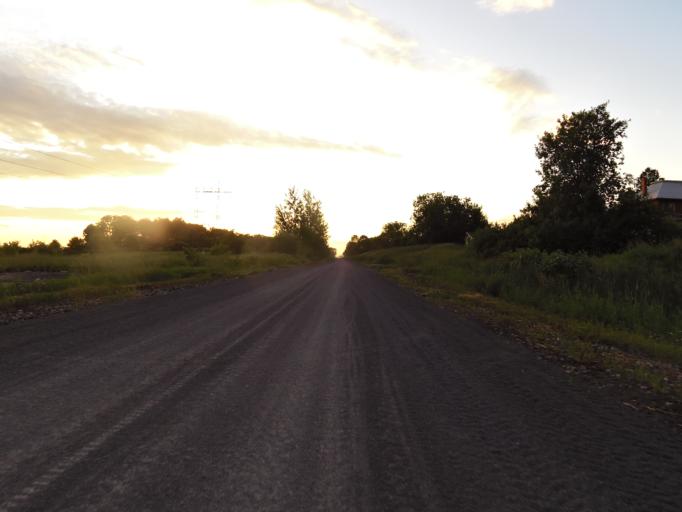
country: CA
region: Ontario
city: Arnprior
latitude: 45.4059
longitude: -76.3282
